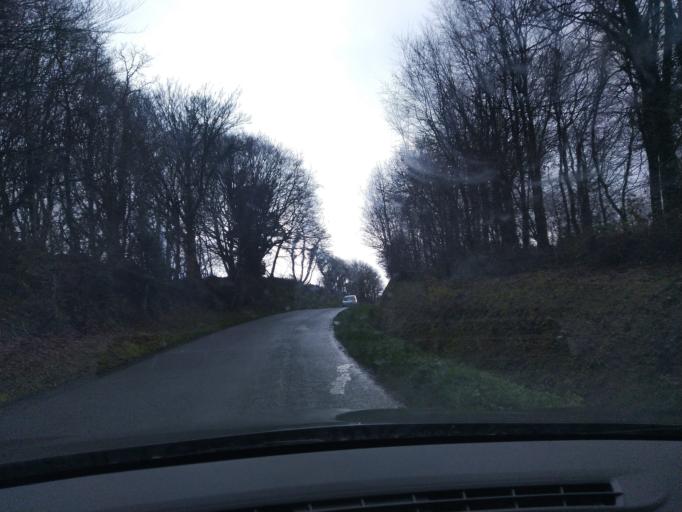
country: FR
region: Brittany
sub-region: Departement du Finistere
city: Guerlesquin
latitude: 48.5003
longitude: -3.5871
